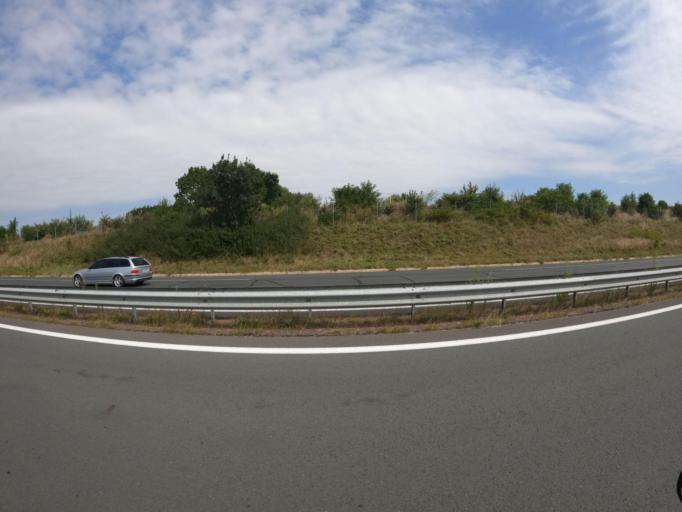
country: FR
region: Poitou-Charentes
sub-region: Departement de la Charente-Maritime
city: Saint-Jean-de-Liversay
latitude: 46.2250
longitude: -0.8641
